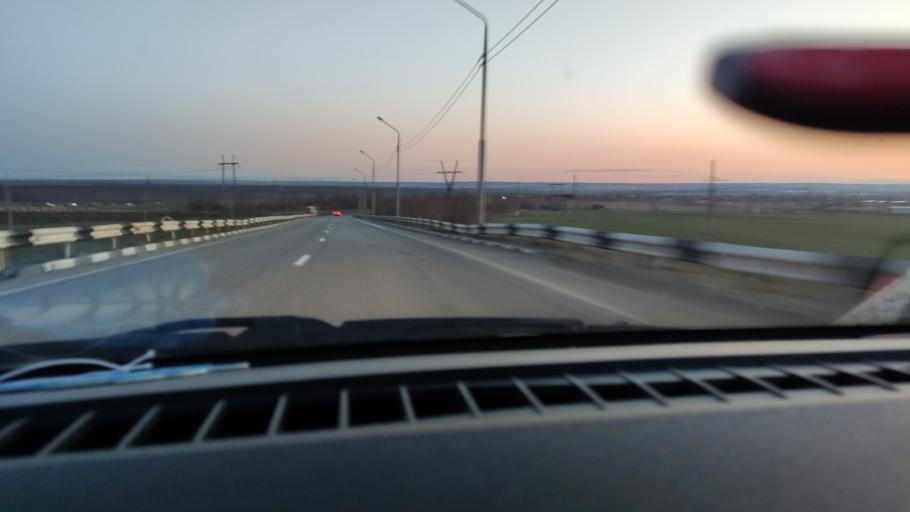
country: RU
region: Saratov
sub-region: Saratovskiy Rayon
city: Saratov
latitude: 51.6699
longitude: 46.0014
